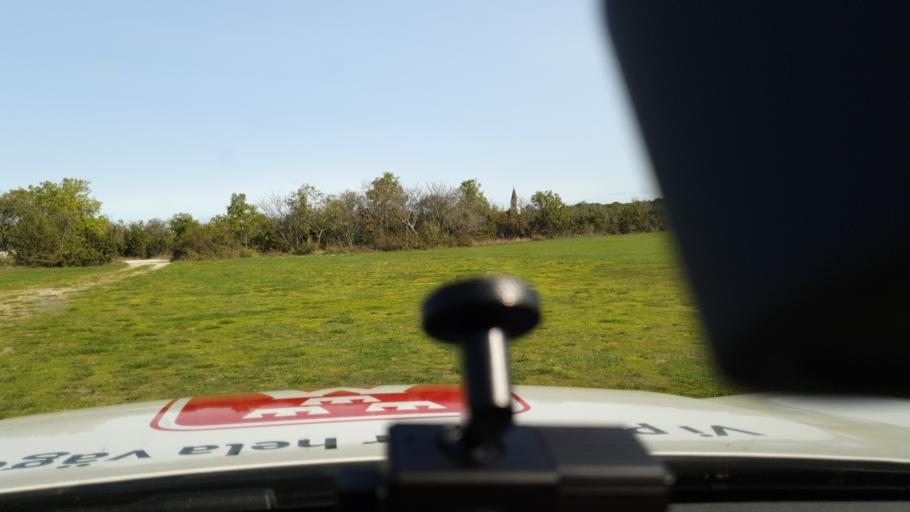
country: SE
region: Gotland
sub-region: Gotland
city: Hemse
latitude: 56.9330
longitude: 18.1701
